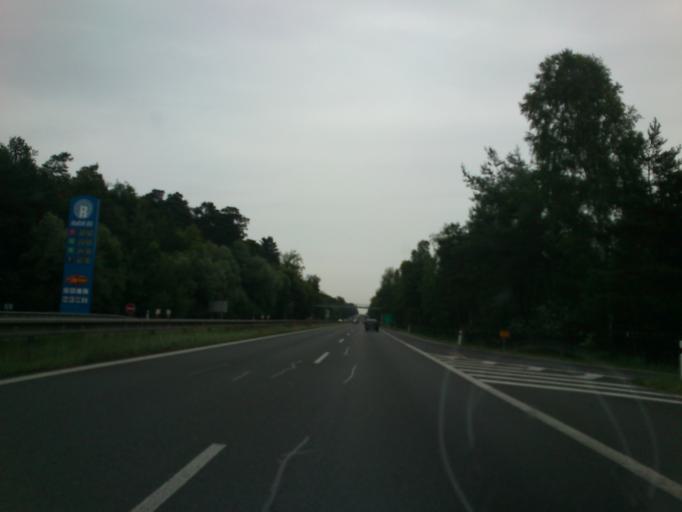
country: CZ
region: Central Bohemia
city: Brandys nad Labem-Stara Boleslav
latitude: 50.2267
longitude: 14.7219
